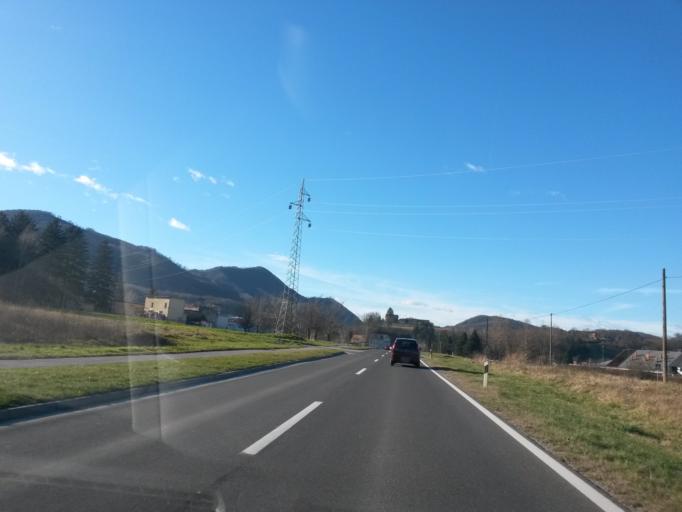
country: HR
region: Varazdinska
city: Lepoglava
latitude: 46.2118
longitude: 16.0406
